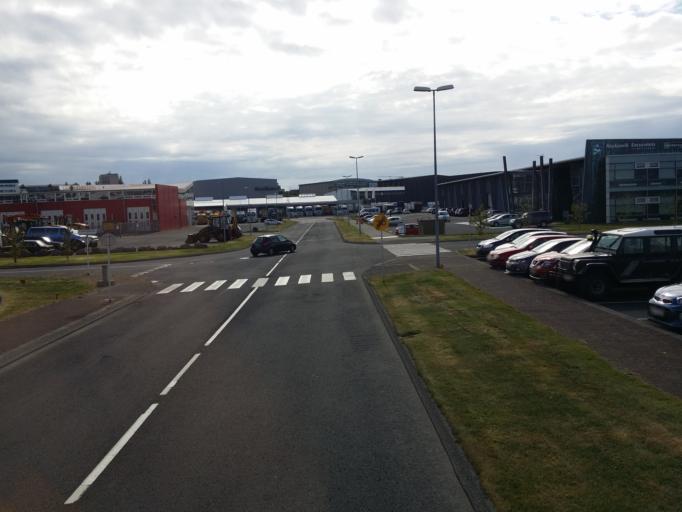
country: IS
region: Capital Region
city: Reykjavik
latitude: 64.1554
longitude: -21.8675
